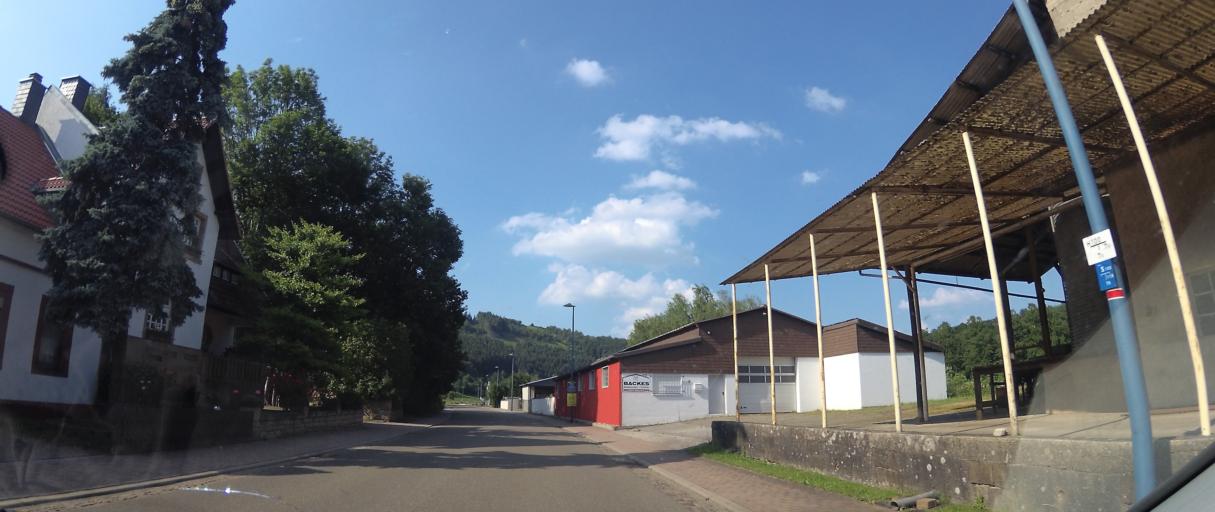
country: DE
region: Rheinland-Pfalz
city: Sankt Julian
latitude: 49.6154
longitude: 7.5314
